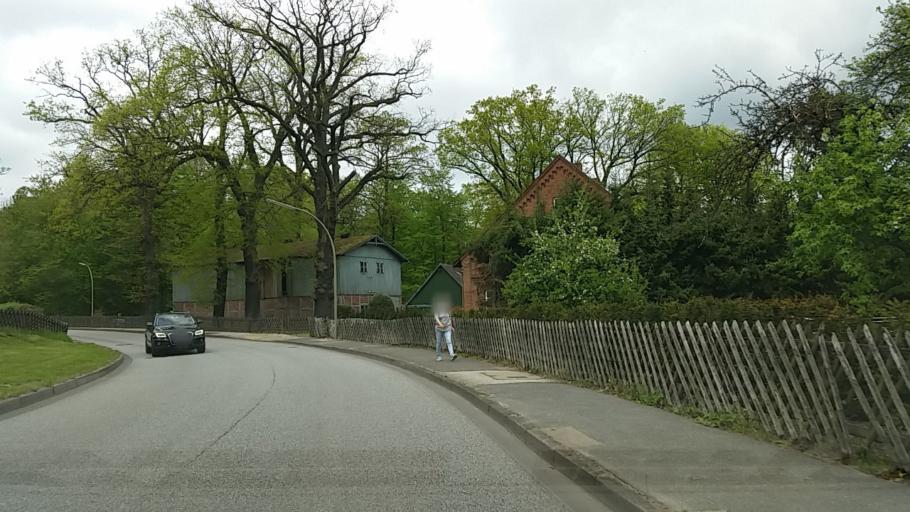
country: DE
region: Hamburg
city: Harburg
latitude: 53.4363
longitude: 10.0082
